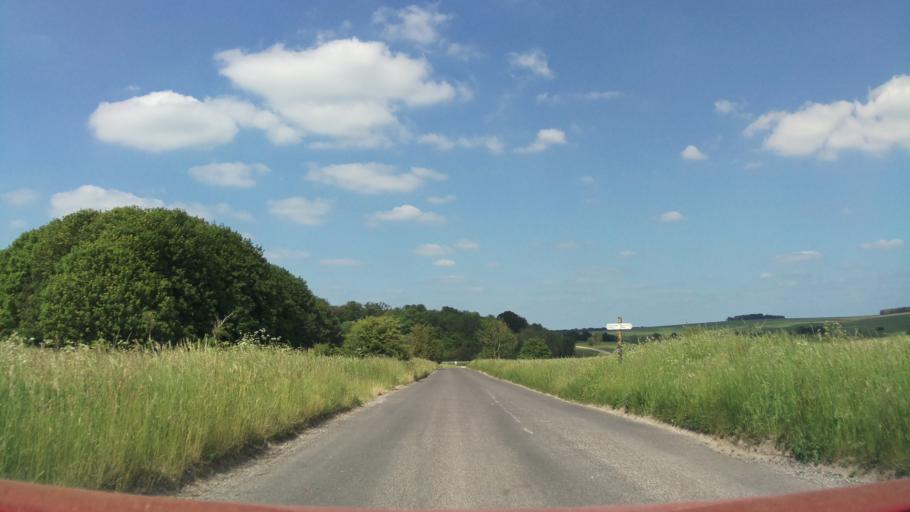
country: GB
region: England
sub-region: Wiltshire
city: Milston
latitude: 51.2553
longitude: -1.7363
